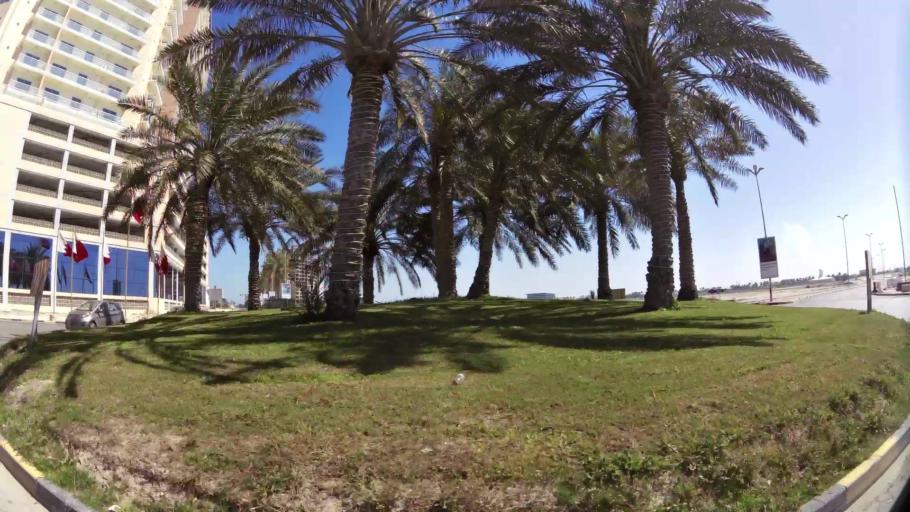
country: BH
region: Muharraq
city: Al Hadd
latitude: 26.2872
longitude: 50.6599
